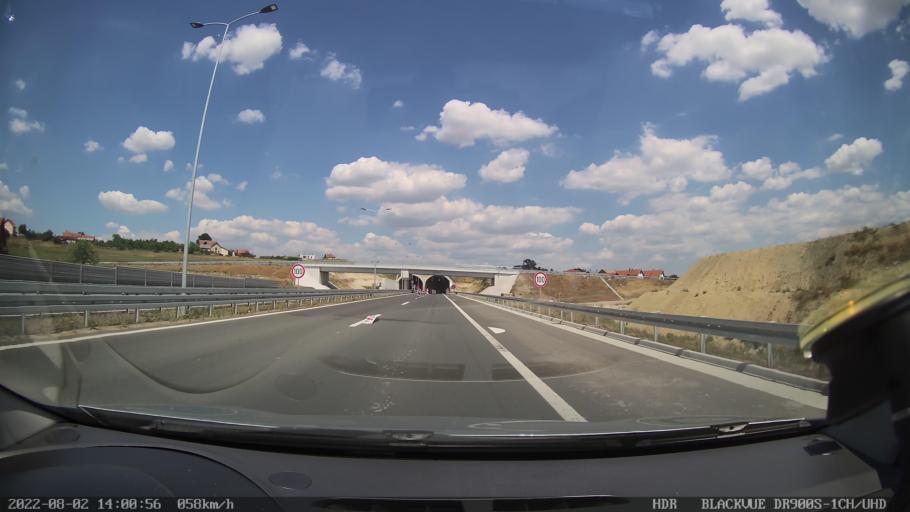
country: RS
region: Central Serbia
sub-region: Moravicki Okrug
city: Cacak
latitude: 43.9239
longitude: 20.3148
